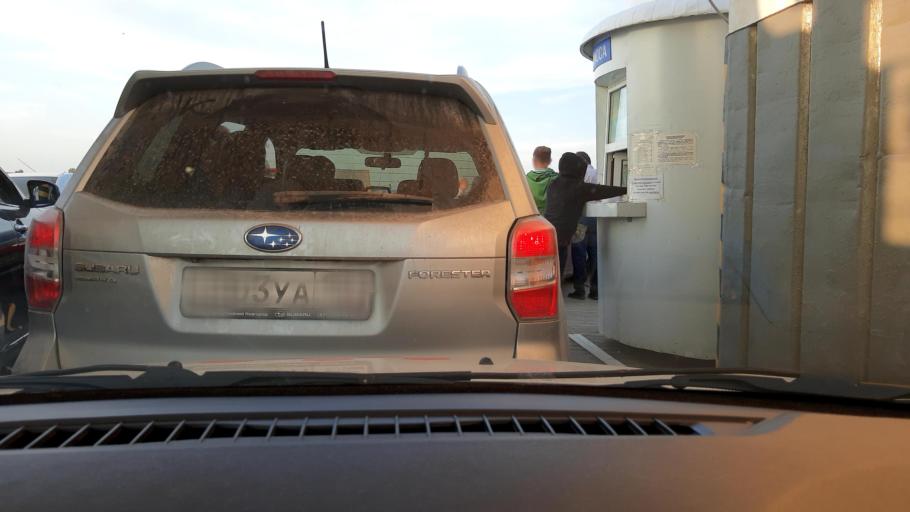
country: RU
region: Nizjnij Novgorod
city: Nizhniy Novgorod
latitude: 56.3360
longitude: 44.0275
